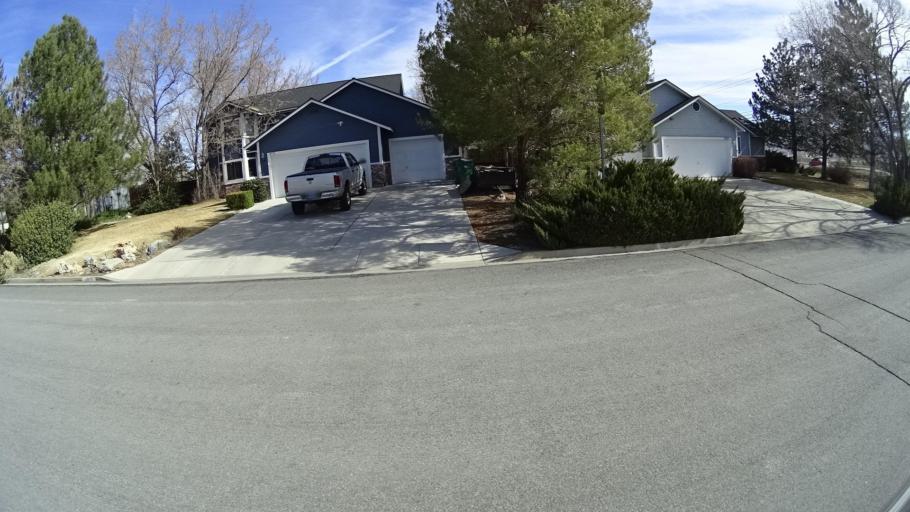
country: US
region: Nevada
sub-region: Washoe County
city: Spanish Springs
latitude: 39.6240
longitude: -119.7243
